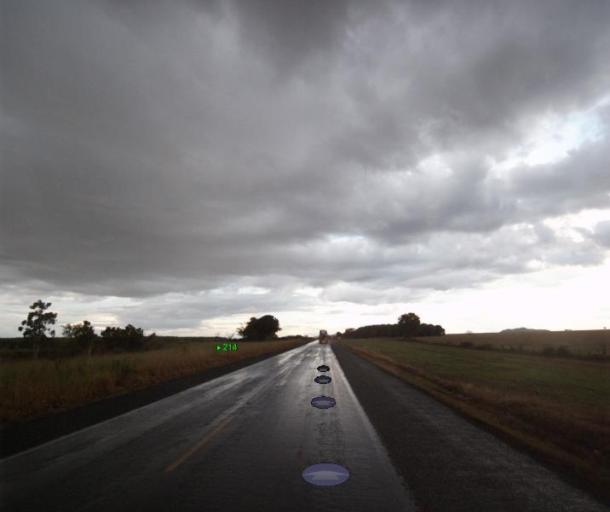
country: BR
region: Goias
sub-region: Uruacu
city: Uruacu
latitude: -14.6457
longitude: -49.1833
